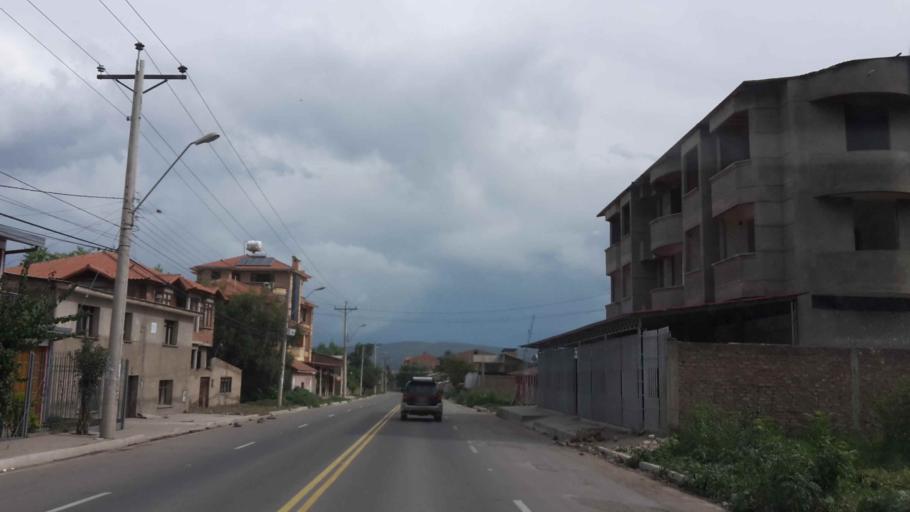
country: BO
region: Cochabamba
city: Cochabamba
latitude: -17.3660
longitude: -66.2526
